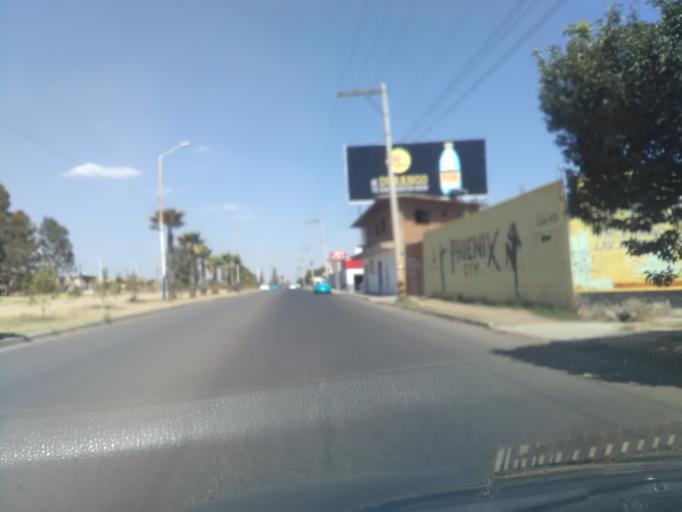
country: MX
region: Durango
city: Victoria de Durango
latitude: 24.0422
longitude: -104.6483
